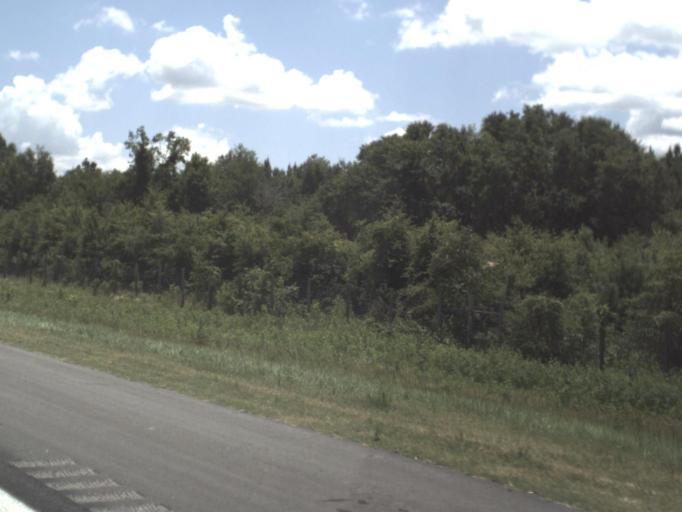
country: US
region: Florida
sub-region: Madison County
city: Madison
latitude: 30.4126
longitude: -83.4289
